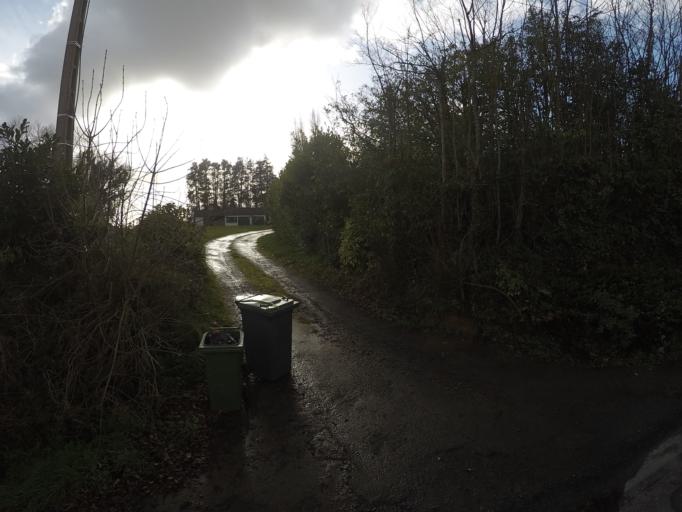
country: FR
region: Brittany
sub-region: Departement des Cotes-d'Armor
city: Goudelin
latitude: 48.6153
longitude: -3.0031
